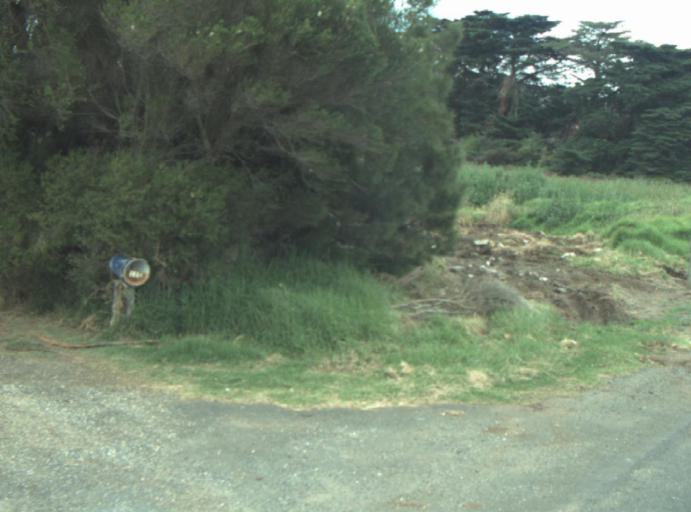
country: AU
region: Victoria
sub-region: Greater Geelong
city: Wandana Heights
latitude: -38.2061
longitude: 144.2897
